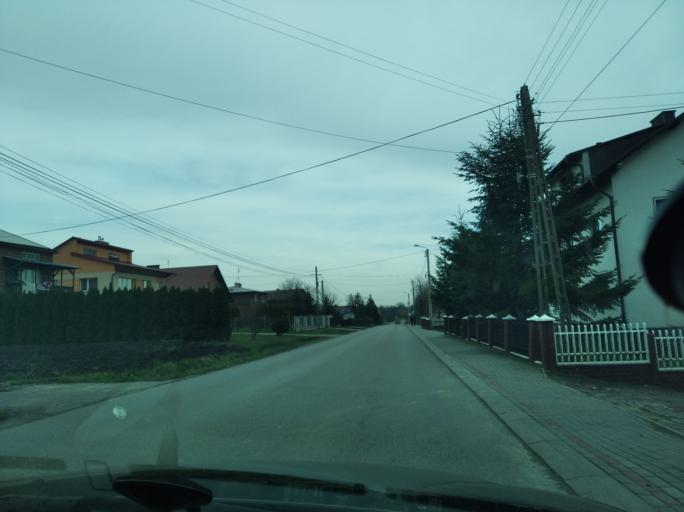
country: PL
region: Subcarpathian Voivodeship
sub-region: Powiat lancucki
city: Wysoka
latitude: 50.0206
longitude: 22.2703
